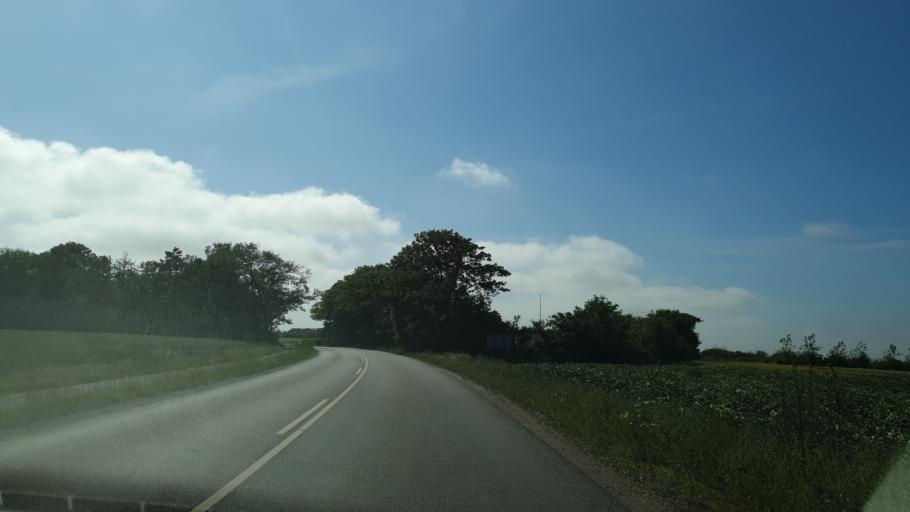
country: DK
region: Central Jutland
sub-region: Ringkobing-Skjern Kommune
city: Ringkobing
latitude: 56.0308
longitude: 8.3424
